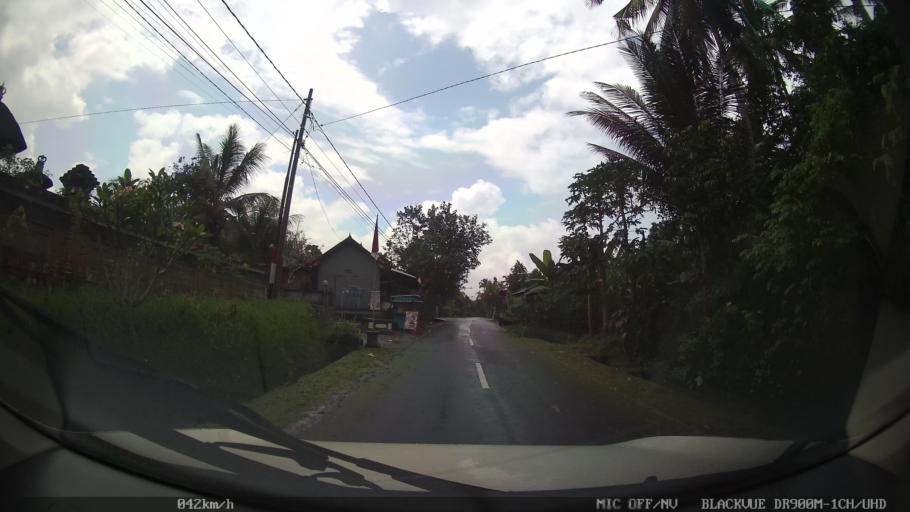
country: ID
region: Bali
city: Banjar Teguan
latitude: -8.4995
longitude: 115.2340
